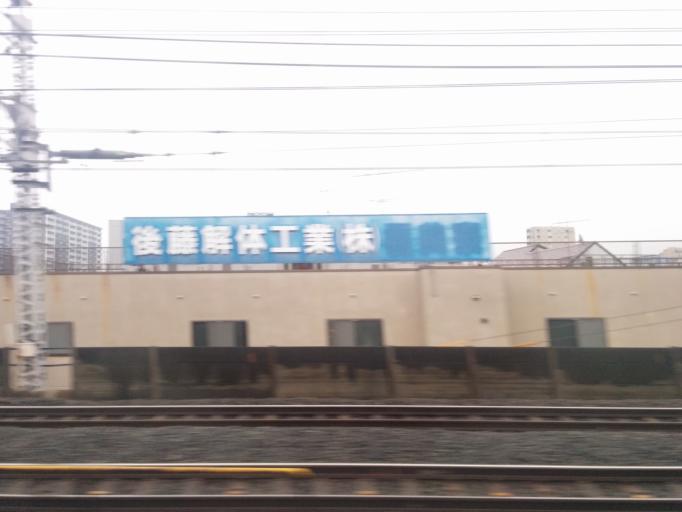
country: JP
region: Tokyo
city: Urayasu
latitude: 35.6996
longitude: 139.8367
